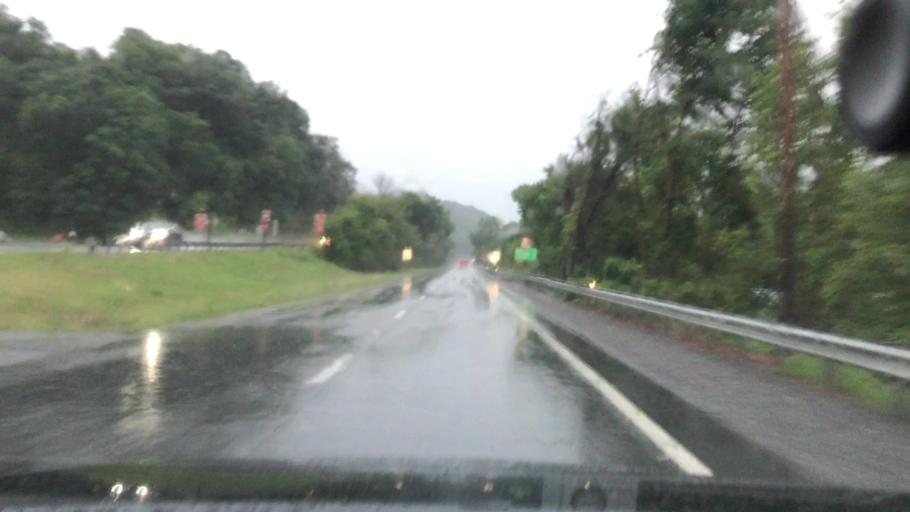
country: US
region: Virginia
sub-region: Giles County
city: Narrows
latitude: 37.3798
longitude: -80.8232
